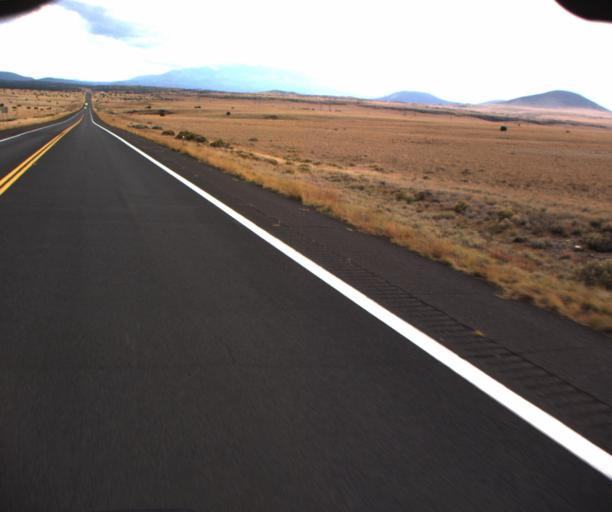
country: US
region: Arizona
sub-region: Coconino County
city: Flagstaff
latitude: 35.5669
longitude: -111.5328
